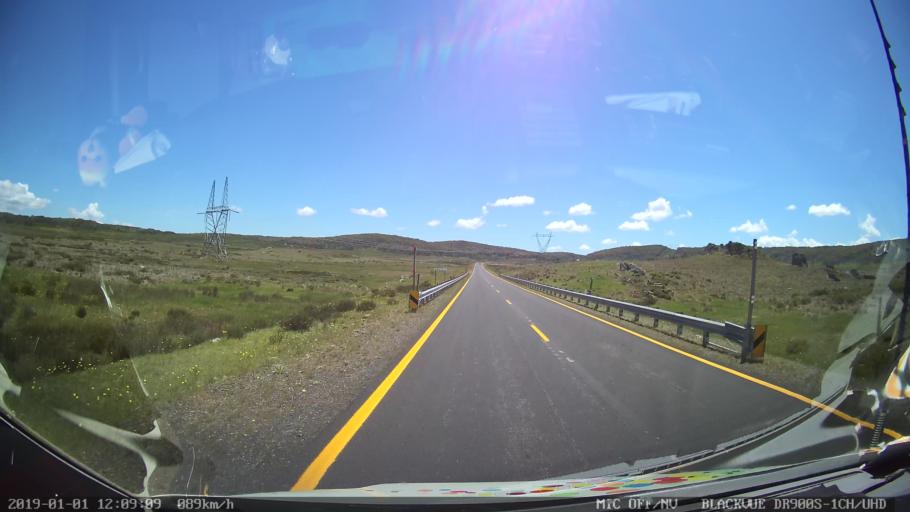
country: AU
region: New South Wales
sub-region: Tumut Shire
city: Tumut
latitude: -35.8110
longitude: 148.4962
